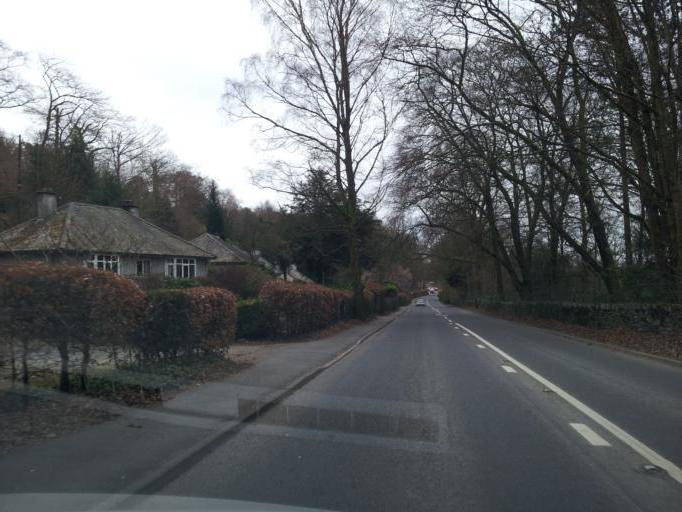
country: GB
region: England
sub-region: Cumbria
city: Windermere
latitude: 54.3731
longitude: -2.9194
